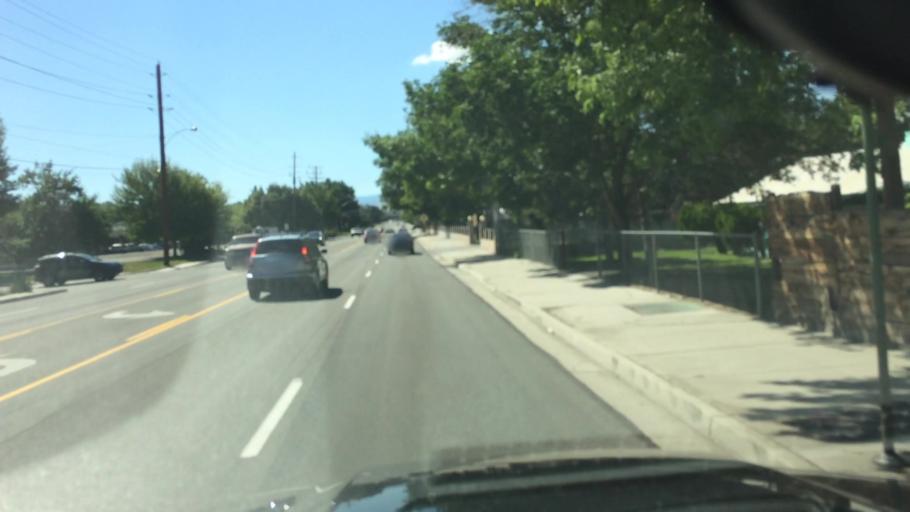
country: US
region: Nevada
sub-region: Washoe County
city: Sparks
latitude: 39.4830
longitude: -119.7777
